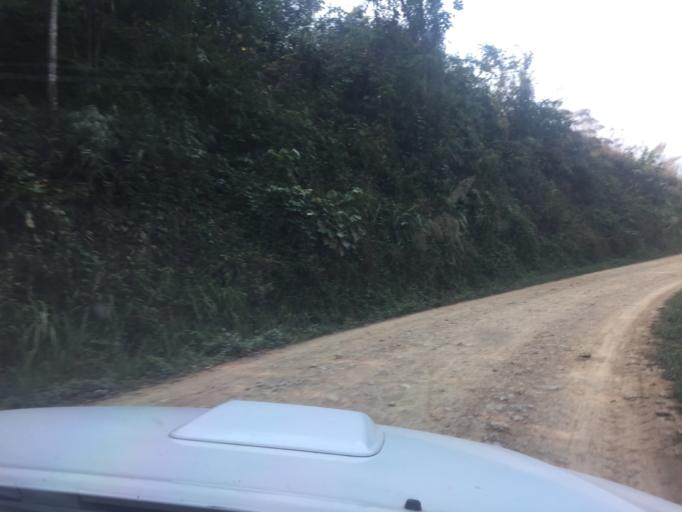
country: TH
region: Phayao
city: Phu Sang
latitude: 19.6510
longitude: 100.5274
